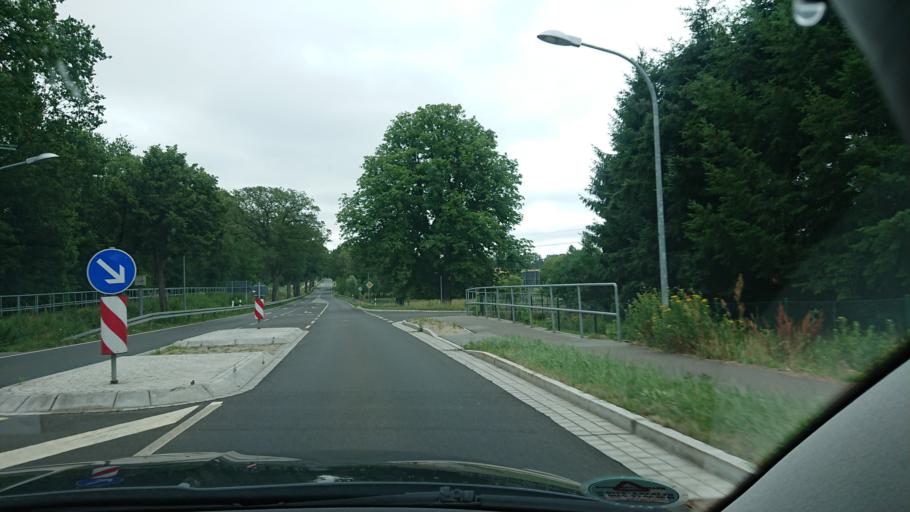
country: DE
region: Brandenburg
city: Bad Wilsnack
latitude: 53.0312
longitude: 11.9714
